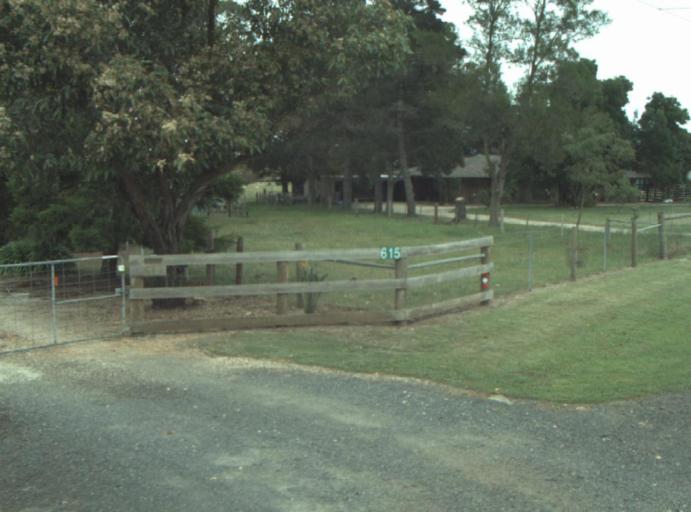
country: AU
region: Victoria
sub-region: Greater Geelong
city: Bell Post Hill
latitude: -38.0646
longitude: 144.3254
